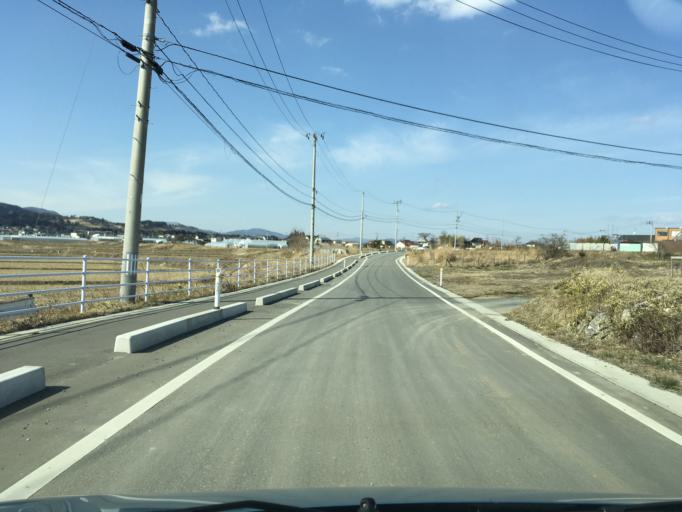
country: JP
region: Iwate
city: Ofunato
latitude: 38.8285
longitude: 141.5858
